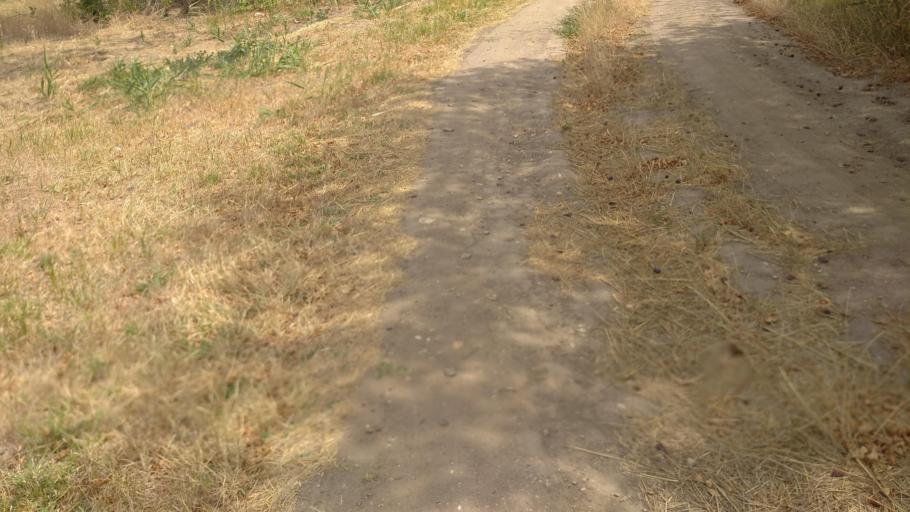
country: HU
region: Bekes
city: Oroshaza
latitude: 46.5595
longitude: 20.6247
